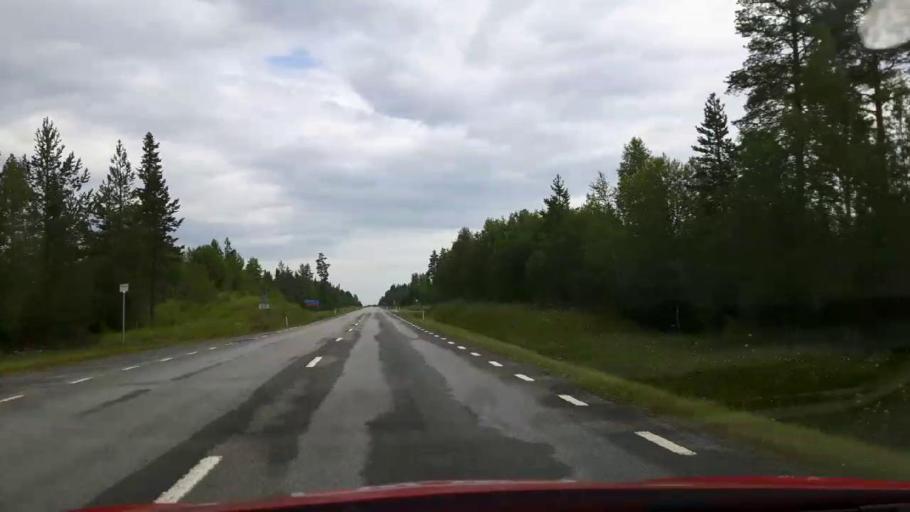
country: SE
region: Jaemtland
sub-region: Stroemsunds Kommun
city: Stroemsund
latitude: 63.6936
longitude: 15.4260
